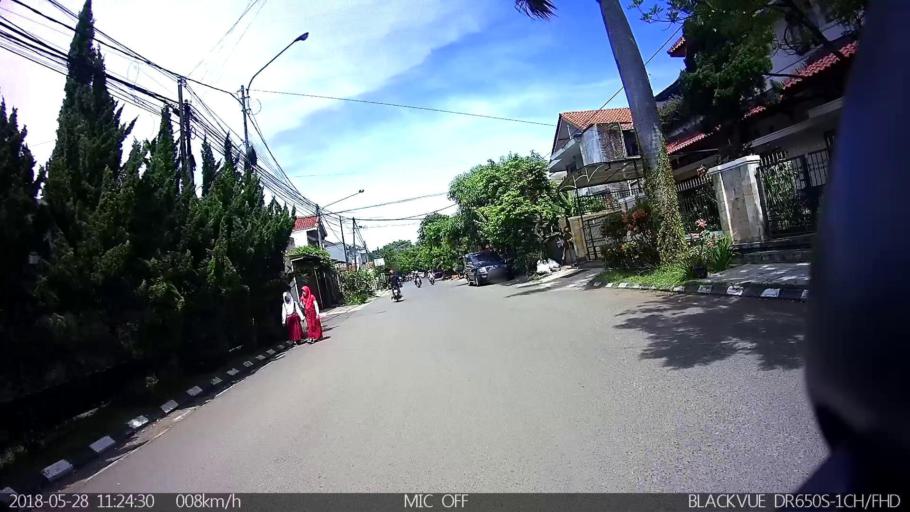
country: ID
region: West Java
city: Bandung
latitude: -6.9095
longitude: 107.6542
